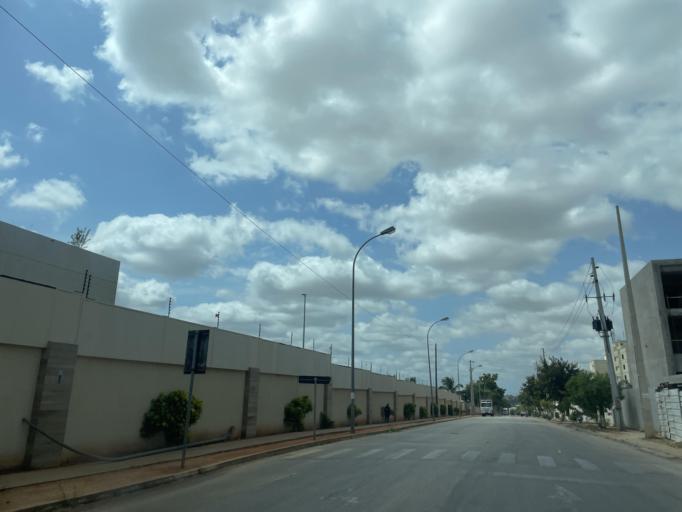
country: AO
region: Luanda
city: Luanda
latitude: -8.9264
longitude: 13.1846
